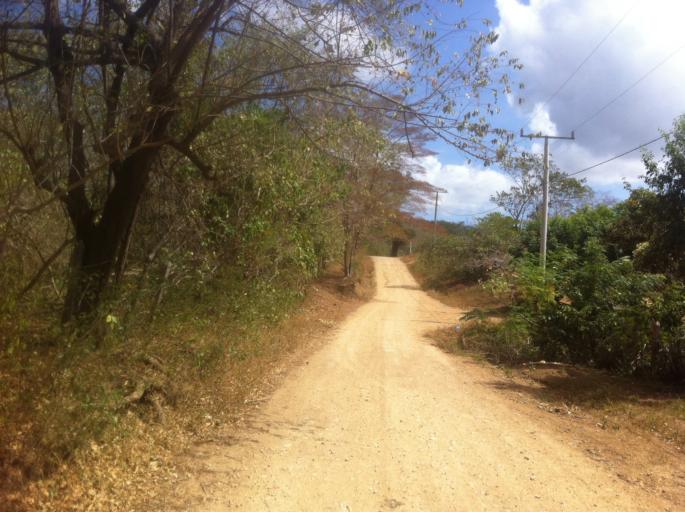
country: NI
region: Rivas
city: Tola
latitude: 11.4026
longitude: -86.0205
